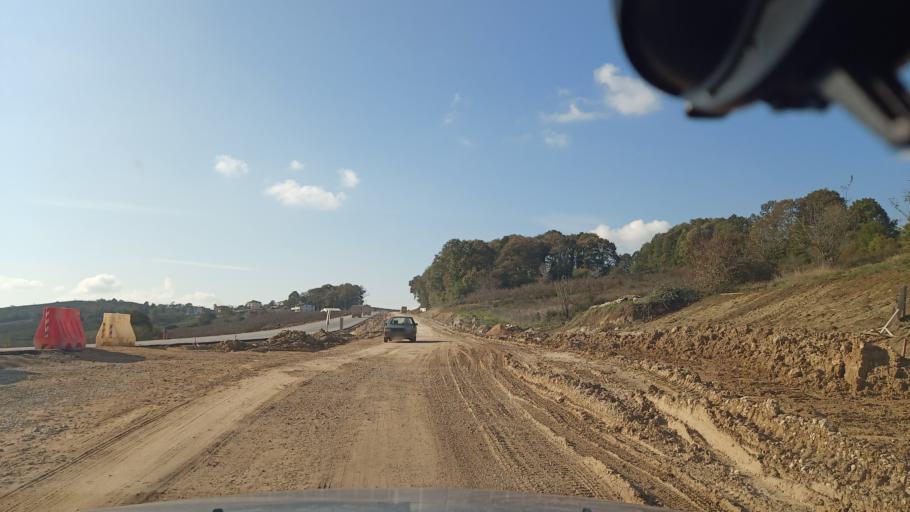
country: TR
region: Sakarya
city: Ferizli
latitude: 41.1017
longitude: 30.4753
